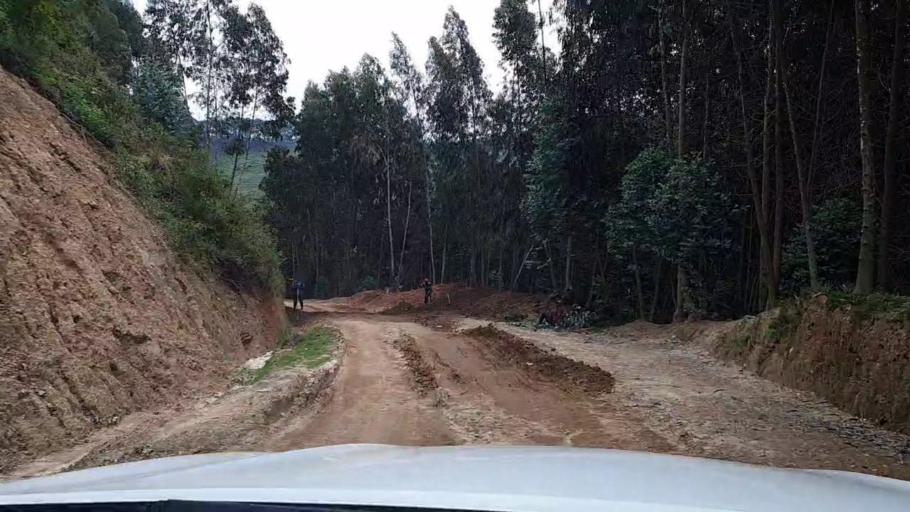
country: RW
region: Western Province
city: Kibuye
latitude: -2.2842
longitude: 29.3688
